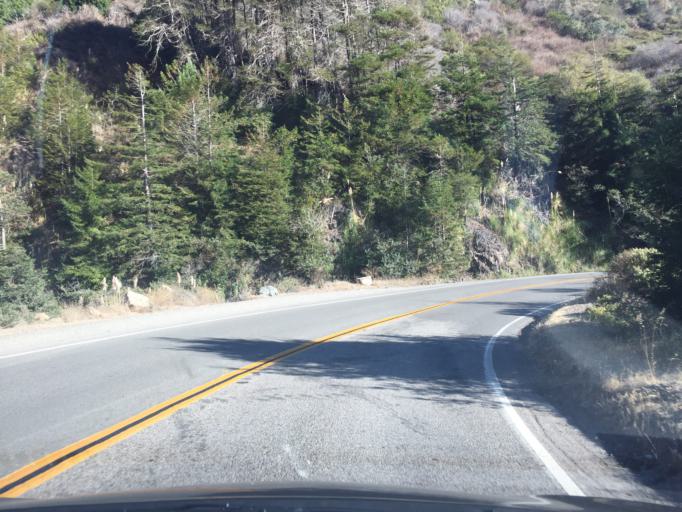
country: US
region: California
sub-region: San Luis Obispo County
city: Cambria
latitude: 35.8362
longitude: -121.3922
